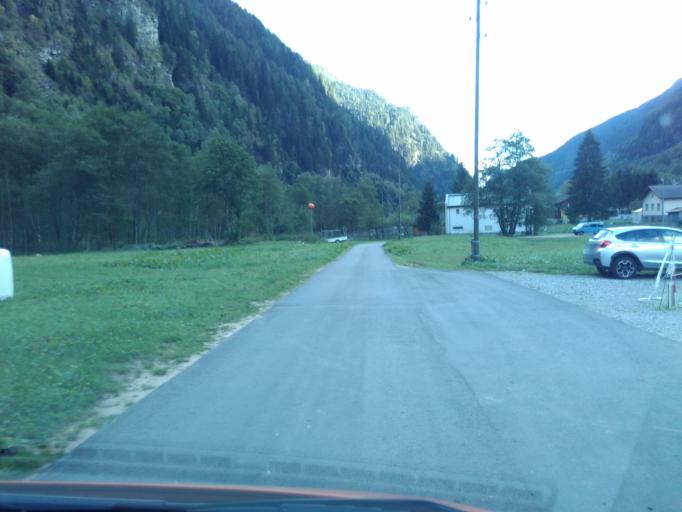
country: CH
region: Grisons
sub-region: Moesa District
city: Cauco
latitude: 46.3641
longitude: 9.1279
